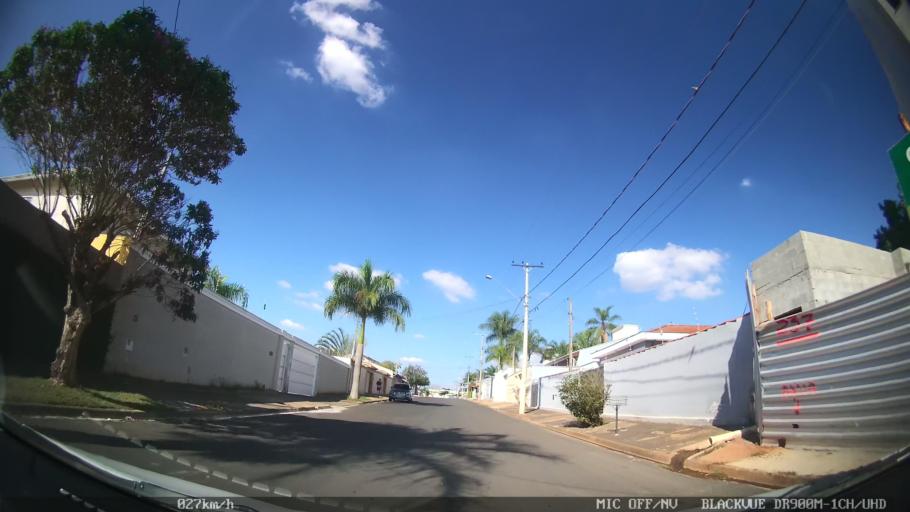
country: BR
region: Sao Paulo
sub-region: Sumare
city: Sumare
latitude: -22.8135
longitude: -47.2865
